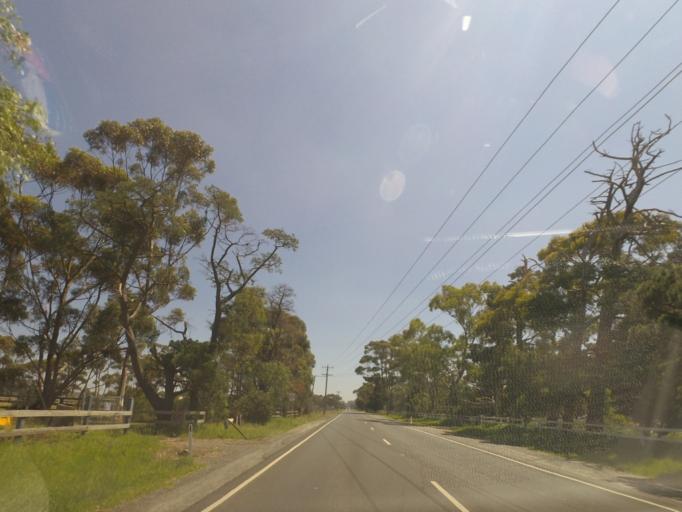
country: AU
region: Victoria
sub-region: Hume
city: Greenvale
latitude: -37.6269
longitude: 144.8370
